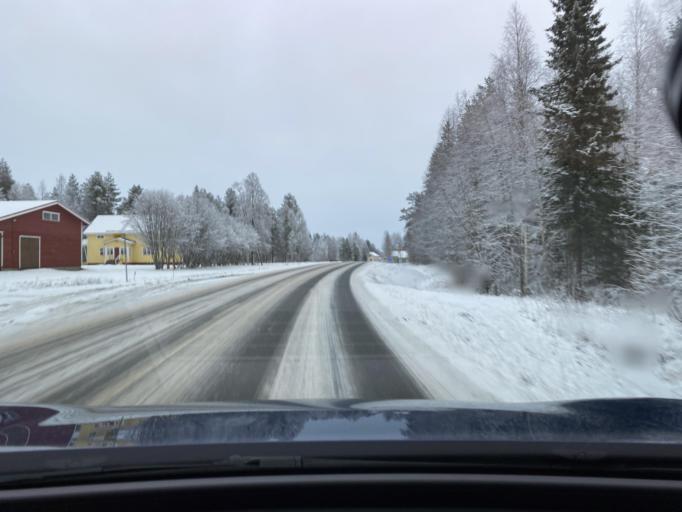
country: FI
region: Lapland
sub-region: Rovaniemi
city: Ranua
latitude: 66.0131
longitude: 26.3144
